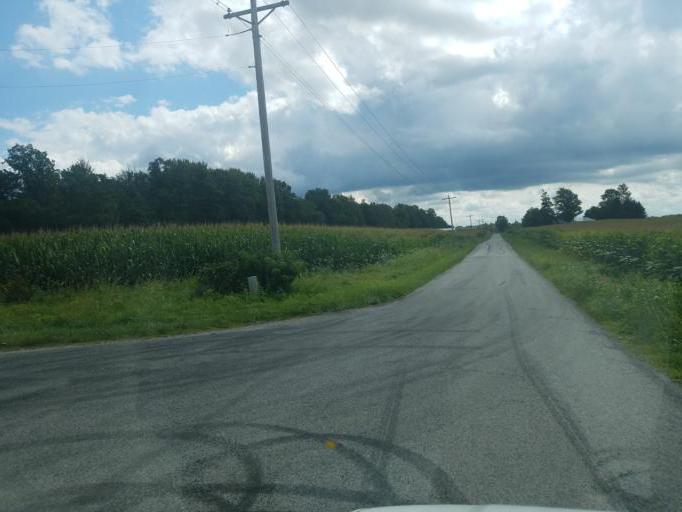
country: US
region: Ohio
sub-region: Huron County
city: Plymouth
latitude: 41.0891
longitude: -82.6298
